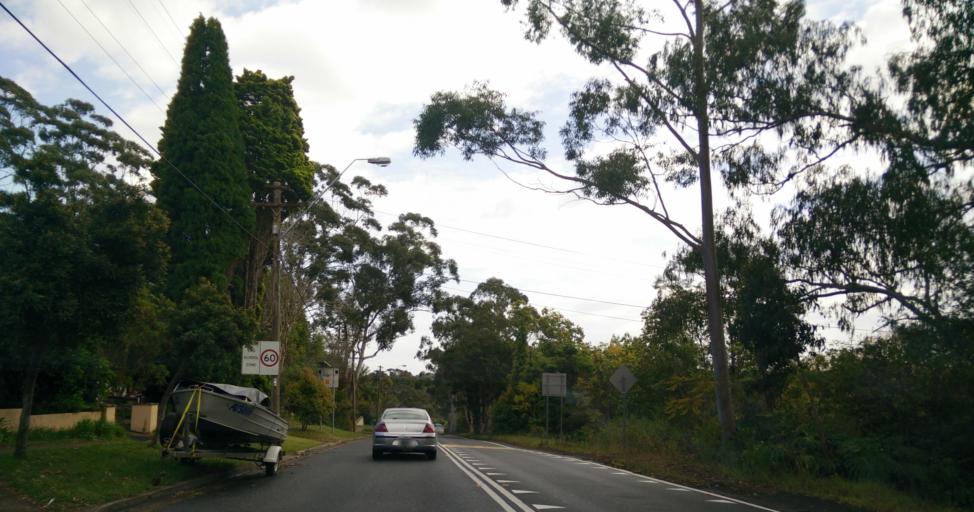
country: AU
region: New South Wales
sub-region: Ku-ring-gai
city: Killara
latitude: -33.7743
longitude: 151.1476
